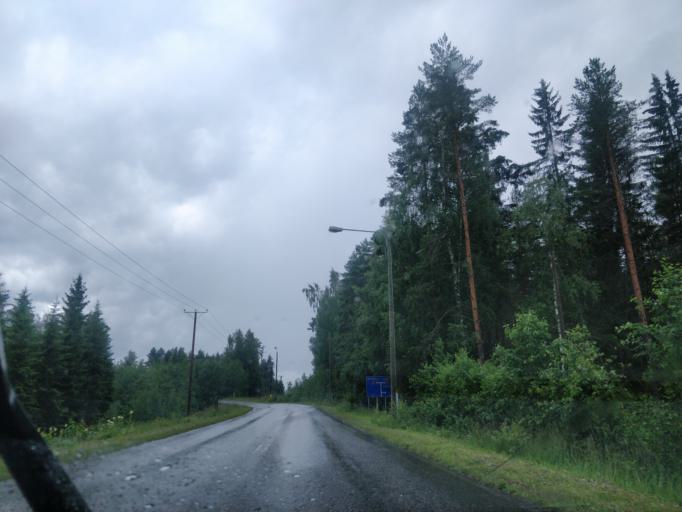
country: FI
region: Southern Savonia
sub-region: Mikkeli
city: Pertunmaa
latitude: 61.3854
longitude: 26.3095
